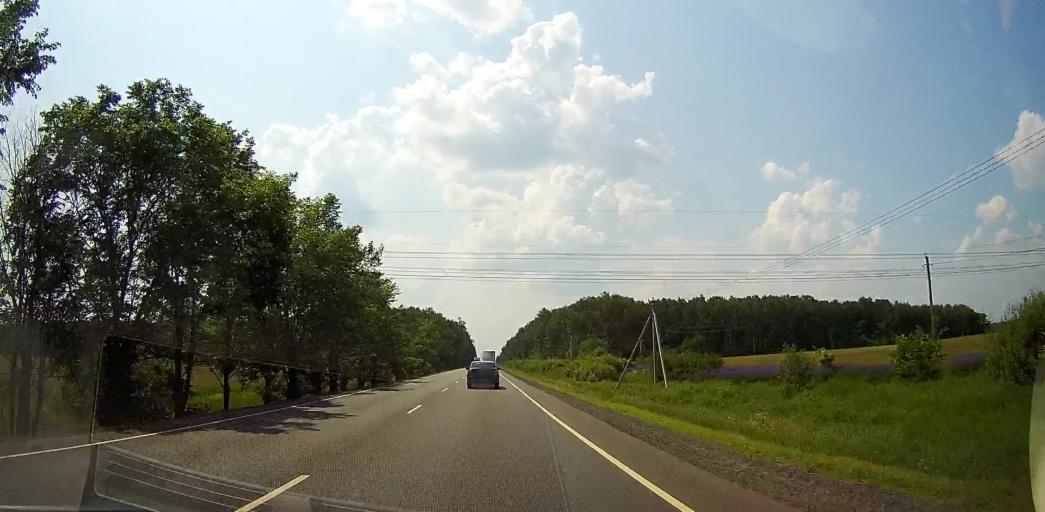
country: RU
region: Moskovskaya
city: Meshcherino
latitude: 55.1413
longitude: 38.2794
